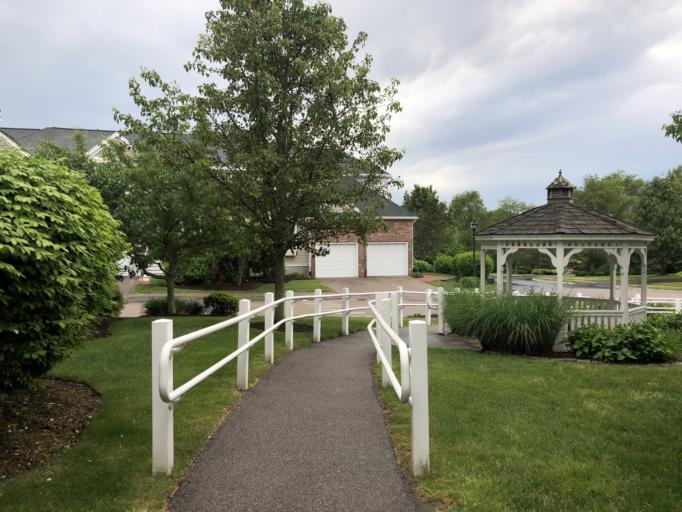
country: US
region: Massachusetts
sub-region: Norfolk County
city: Stoughton
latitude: 42.1475
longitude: -71.0999
